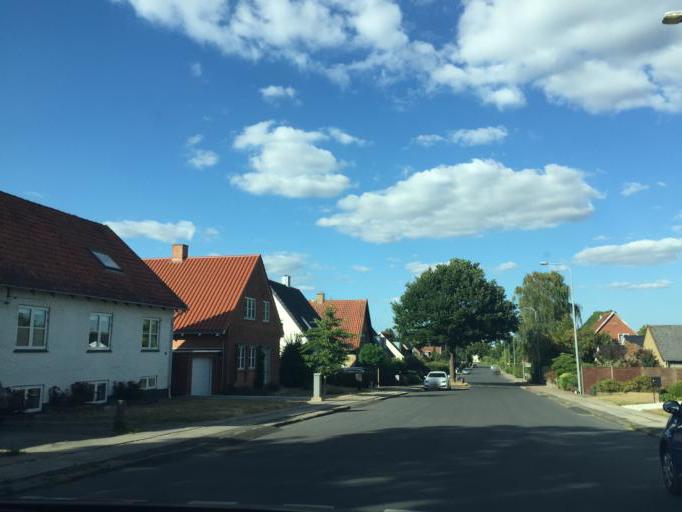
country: DK
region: South Denmark
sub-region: Odense Kommune
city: Odense
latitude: 55.3734
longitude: 10.3608
